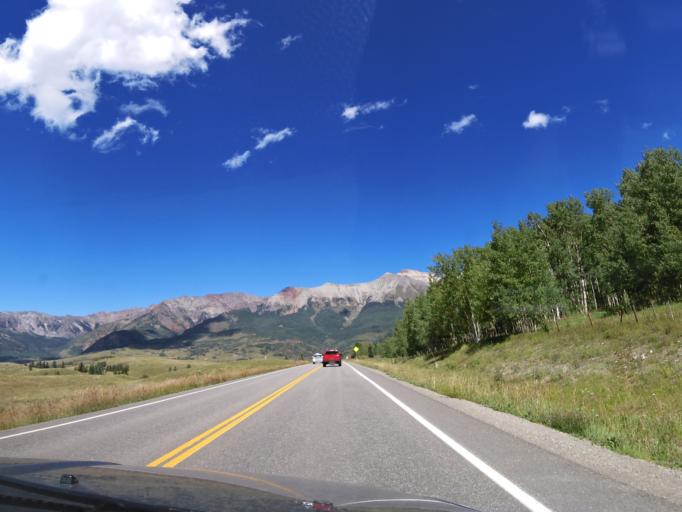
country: US
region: Colorado
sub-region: San Miguel County
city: Mountain Village
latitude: 37.9229
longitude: -107.8836
